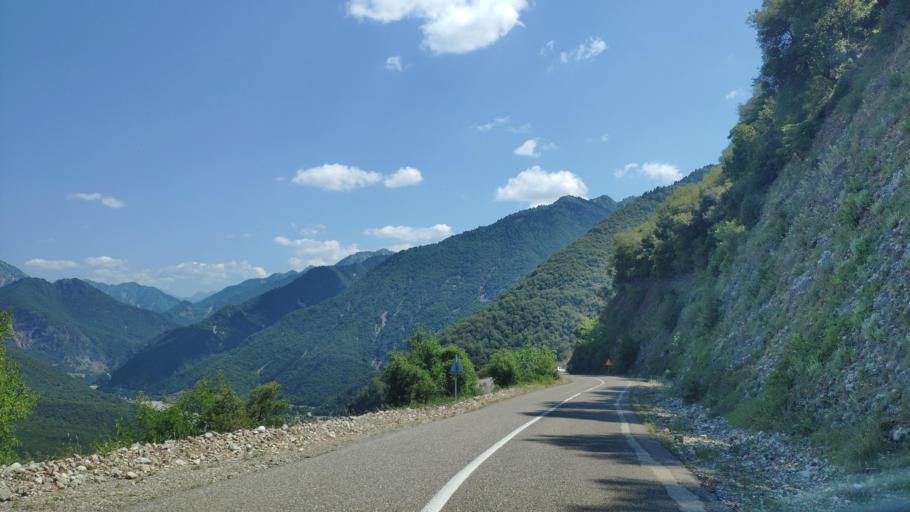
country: GR
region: Central Greece
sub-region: Nomos Evrytanias
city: Kerasochori
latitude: 39.0079
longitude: 21.5938
